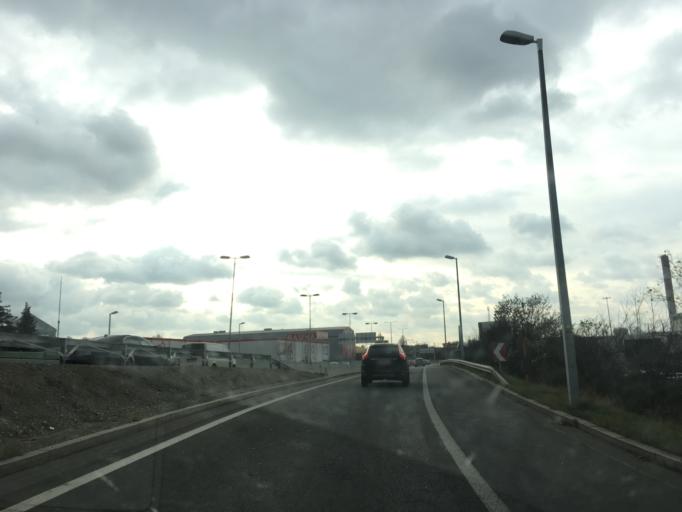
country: AT
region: Lower Austria
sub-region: Politischer Bezirk Wien-Umgebung
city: Gerasdorf bei Wien
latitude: 48.2391
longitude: 16.4591
